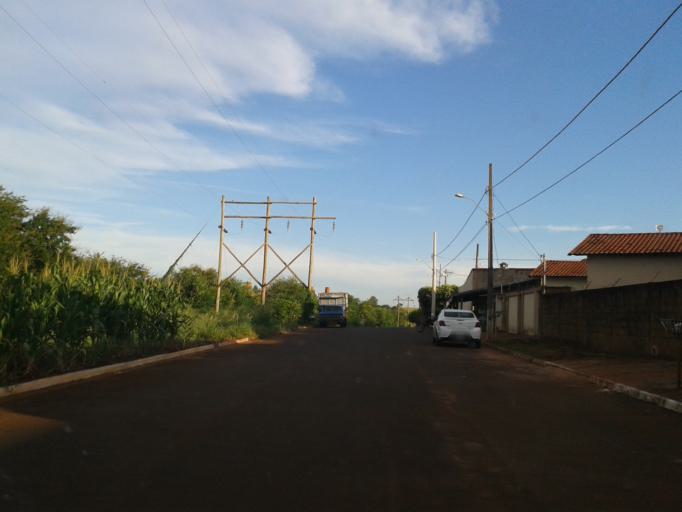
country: BR
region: Minas Gerais
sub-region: Capinopolis
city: Capinopolis
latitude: -18.6902
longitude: -49.5638
